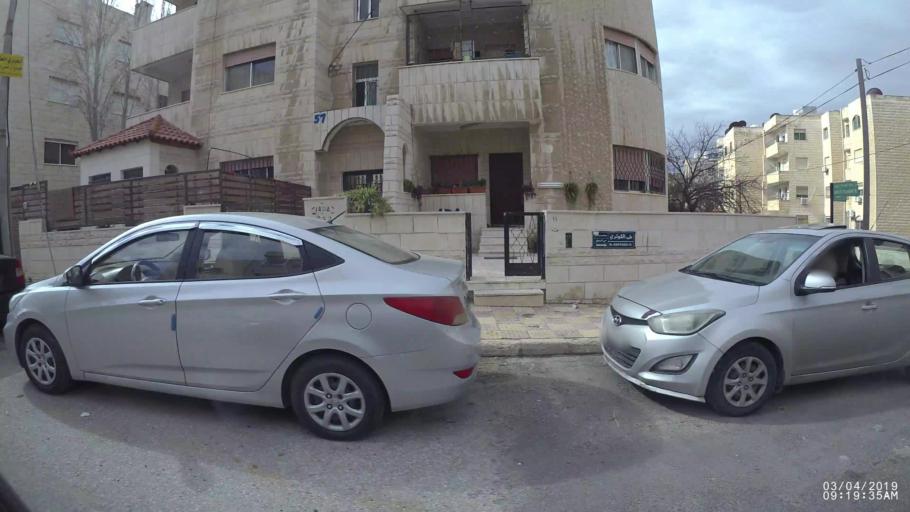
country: JO
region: Amman
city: Wadi as Sir
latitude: 31.9483
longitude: 35.8429
